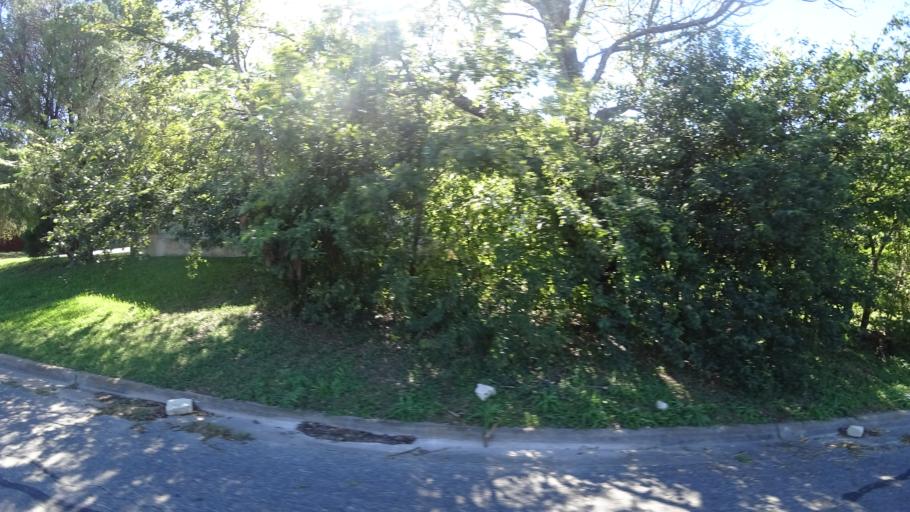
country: US
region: Texas
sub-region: Travis County
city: Austin
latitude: 30.2883
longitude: -97.7125
